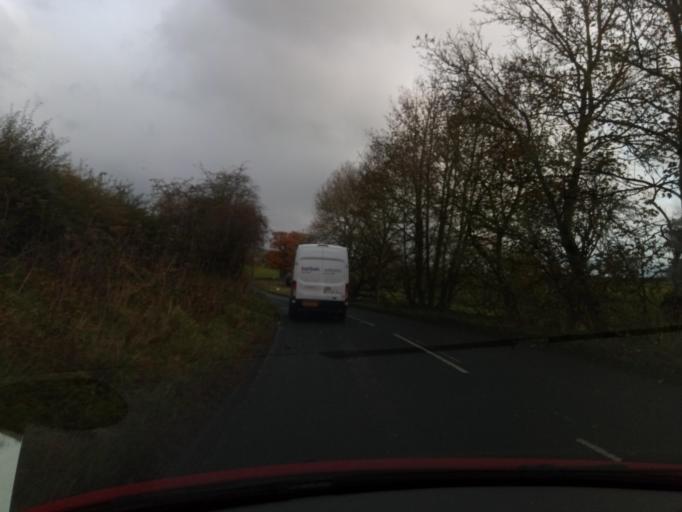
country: GB
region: England
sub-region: Northumberland
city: Birtley
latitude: 55.0548
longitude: -2.1865
